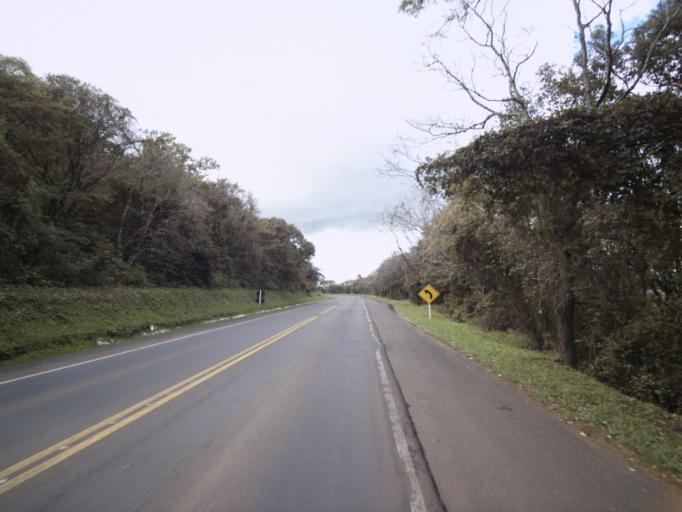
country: BR
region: Santa Catarina
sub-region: Concordia
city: Concordia
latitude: -27.2630
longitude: -51.9568
